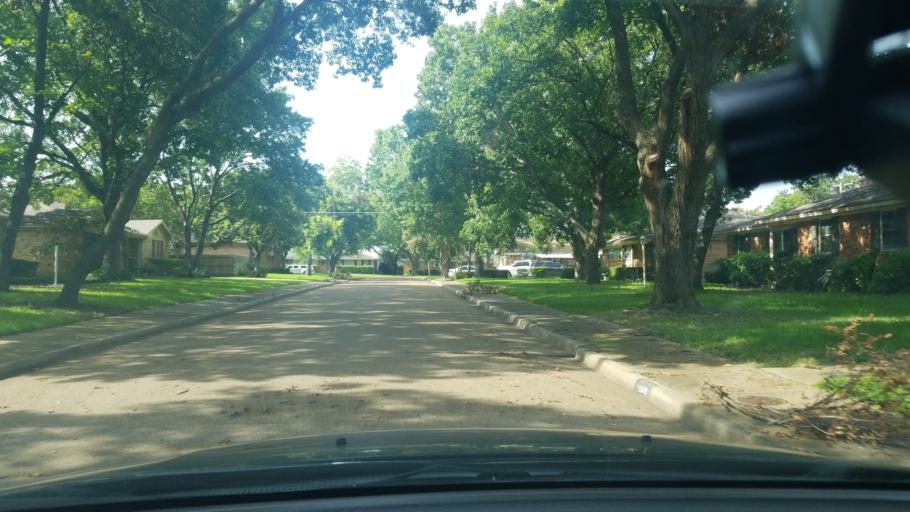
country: US
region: Texas
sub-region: Dallas County
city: Highland Park
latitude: 32.7971
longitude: -96.7019
